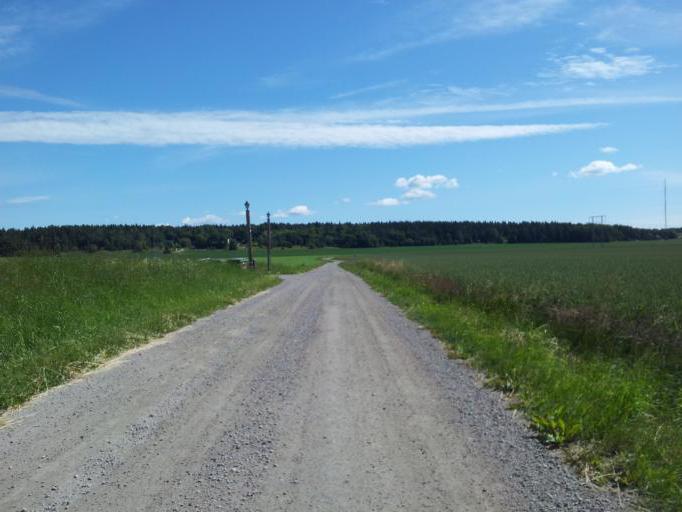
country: SE
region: Uppsala
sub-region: Uppsala Kommun
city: Saevja
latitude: 59.8633
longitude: 17.7270
